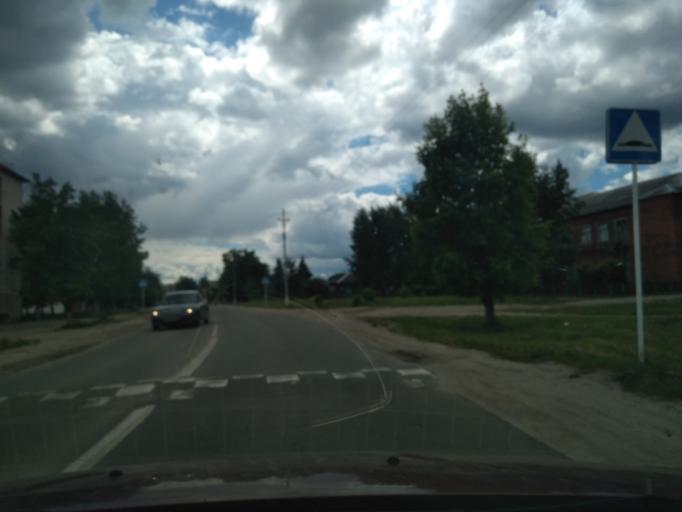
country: RU
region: Vladimir
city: Melenki
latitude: 55.3379
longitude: 41.6126
